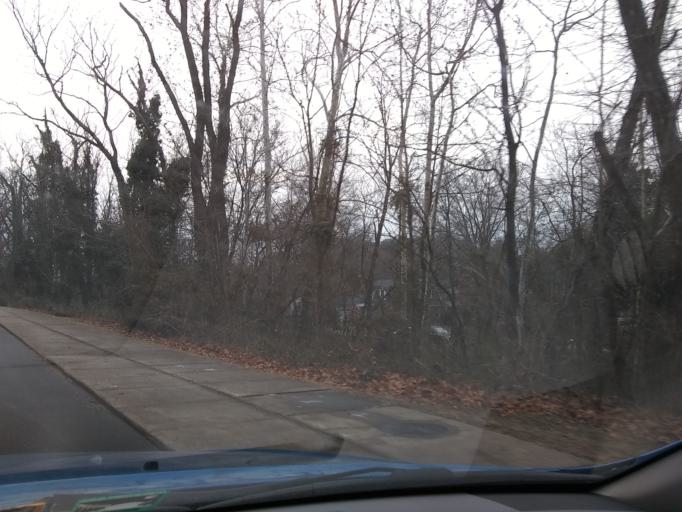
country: US
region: Virginia
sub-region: Fairfax County
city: Huntington
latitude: 38.8122
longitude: -77.0755
